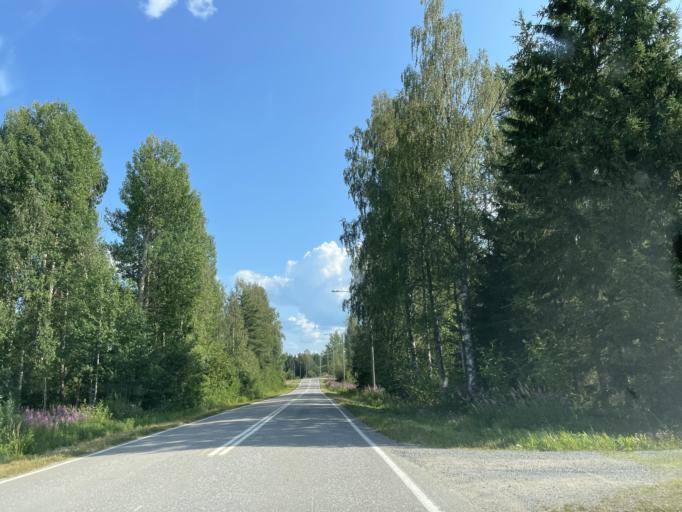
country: FI
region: Central Finland
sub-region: Saarijaervi-Viitasaari
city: Pihtipudas
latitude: 63.3605
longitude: 25.7474
